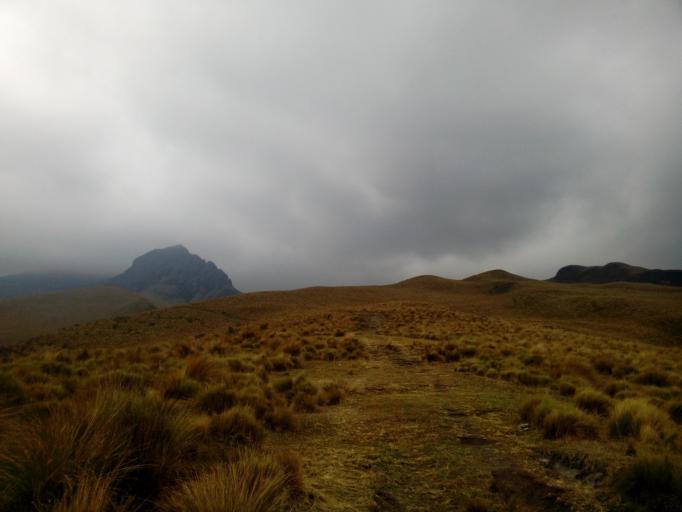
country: EC
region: Pichincha
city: Machachi
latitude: -0.5552
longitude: -78.5301
